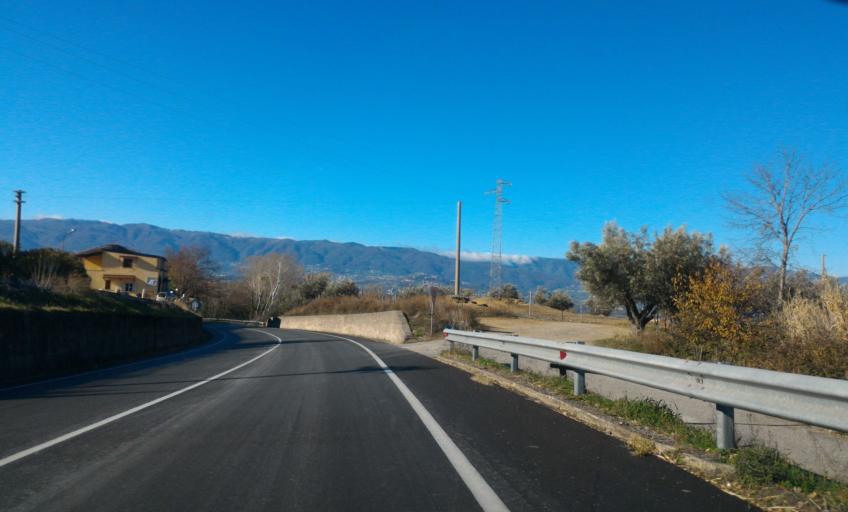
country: IT
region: Calabria
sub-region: Provincia di Cosenza
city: Zumpano
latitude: 39.2993
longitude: 16.2870
